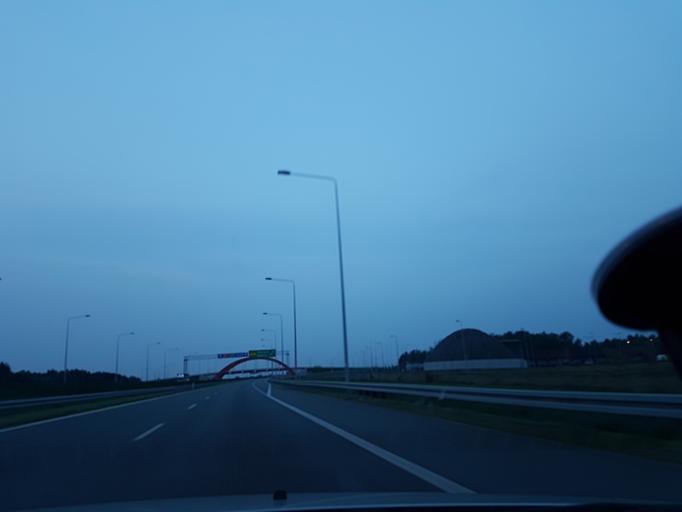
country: PL
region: Lodz Voivodeship
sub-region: Powiat leczycki
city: Piatek
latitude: 52.0684
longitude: 19.5351
